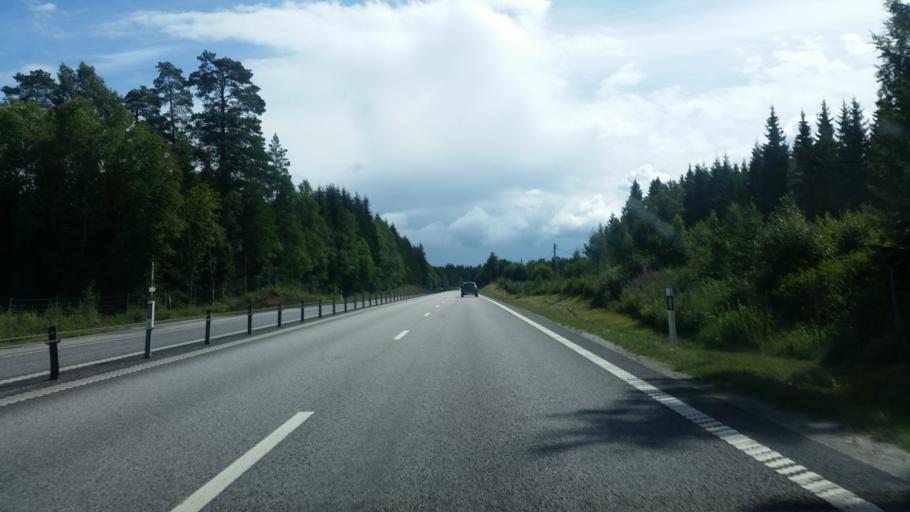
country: SE
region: Joenkoeping
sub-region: Mullsjo Kommun
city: Mullsjoe
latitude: 57.7742
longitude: 13.6926
